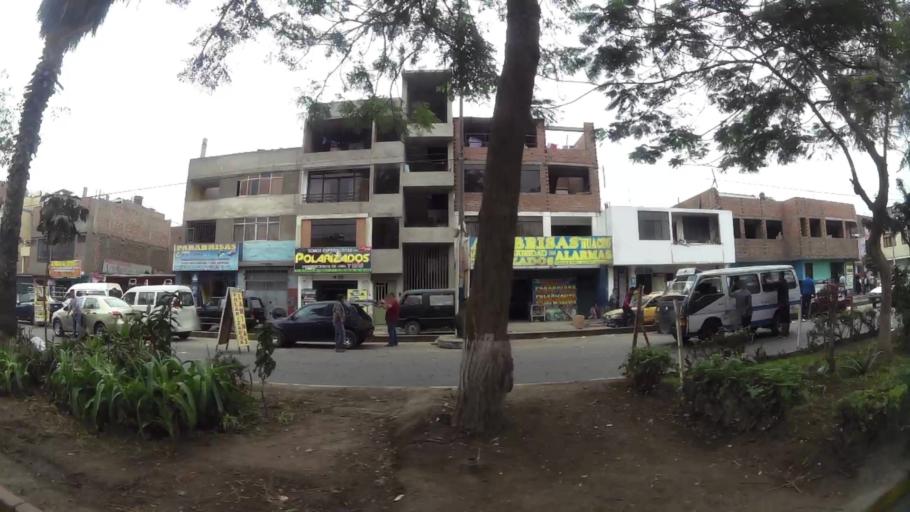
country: PE
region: Lima
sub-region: Lima
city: Independencia
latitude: -11.9834
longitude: -77.0596
